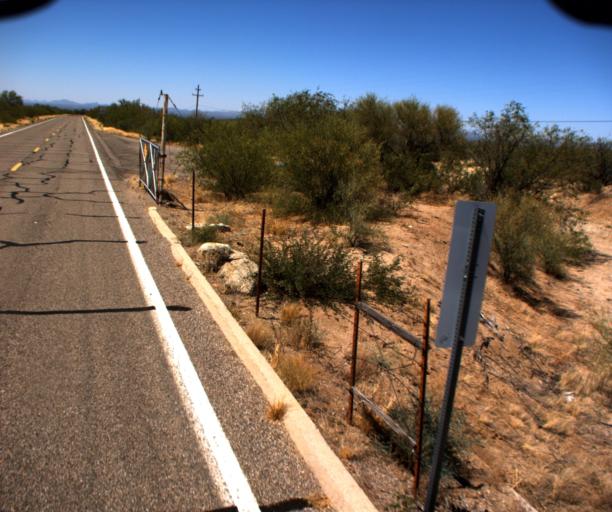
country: US
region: Arizona
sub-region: Pima County
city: Three Points
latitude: 32.0223
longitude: -111.5766
